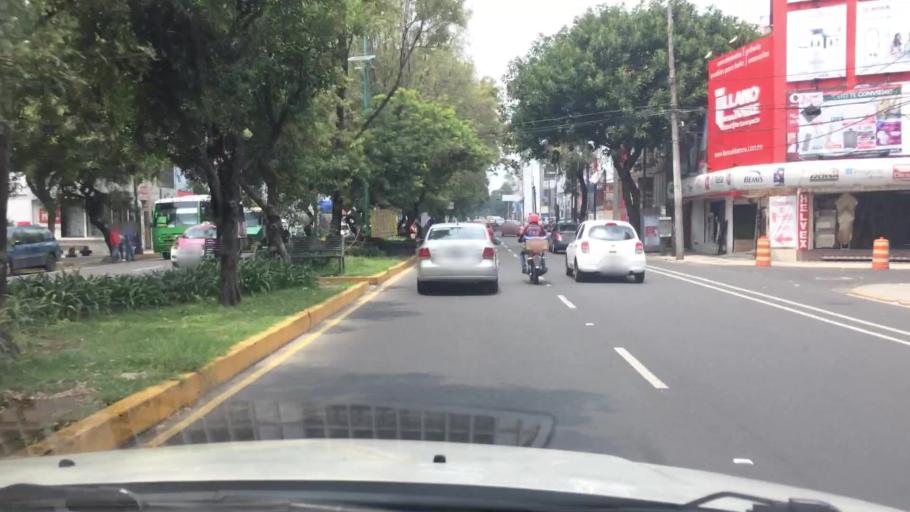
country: MX
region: Mexico City
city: Coyoacan
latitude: 19.3645
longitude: -99.1550
